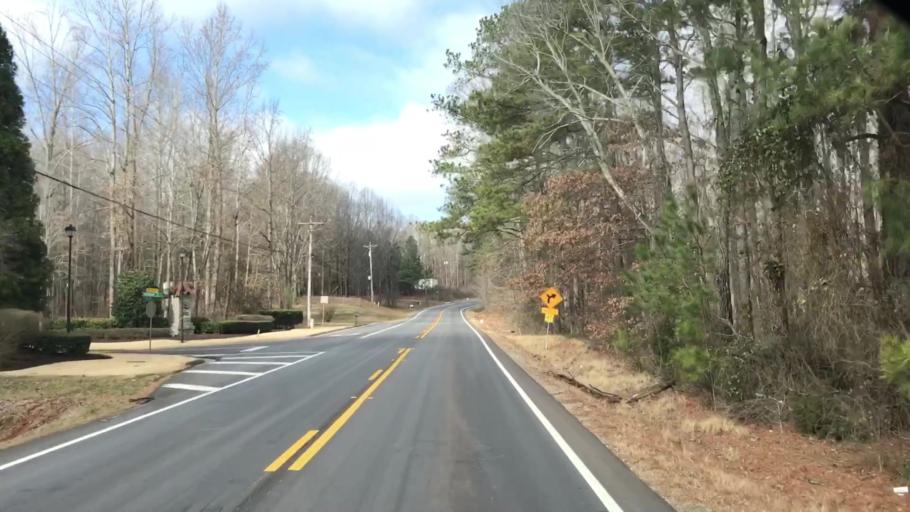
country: US
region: Georgia
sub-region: Jackson County
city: Braselton
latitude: 34.1399
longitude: -83.8366
